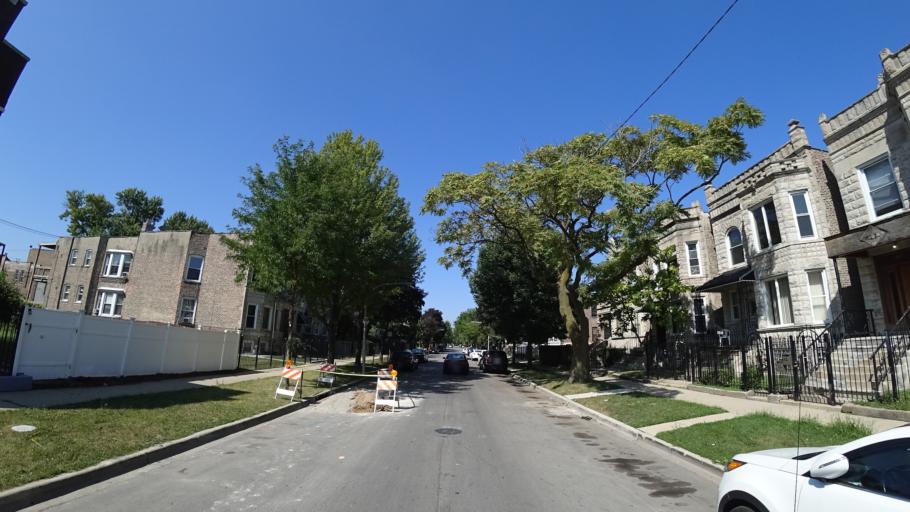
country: US
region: Illinois
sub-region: Cook County
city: Cicero
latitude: 41.8717
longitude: -87.7159
